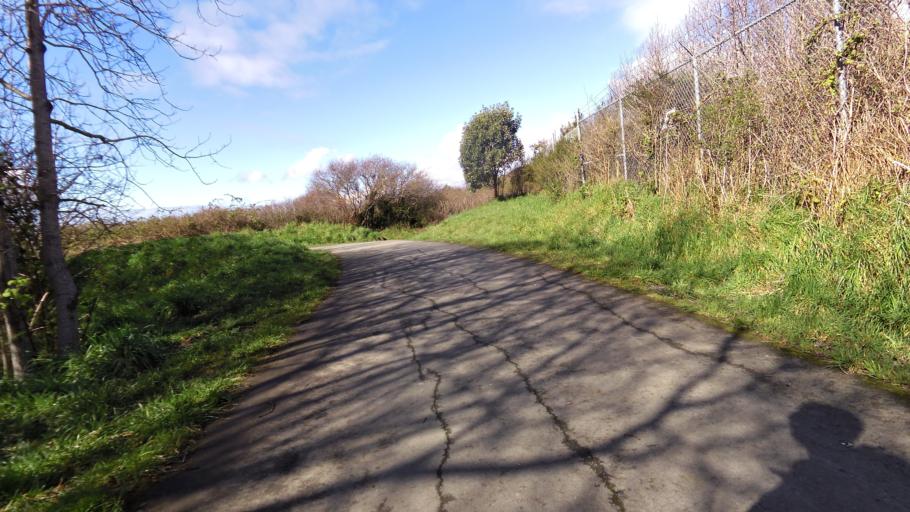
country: CA
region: British Columbia
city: Victoria
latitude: 48.4182
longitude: -123.4082
